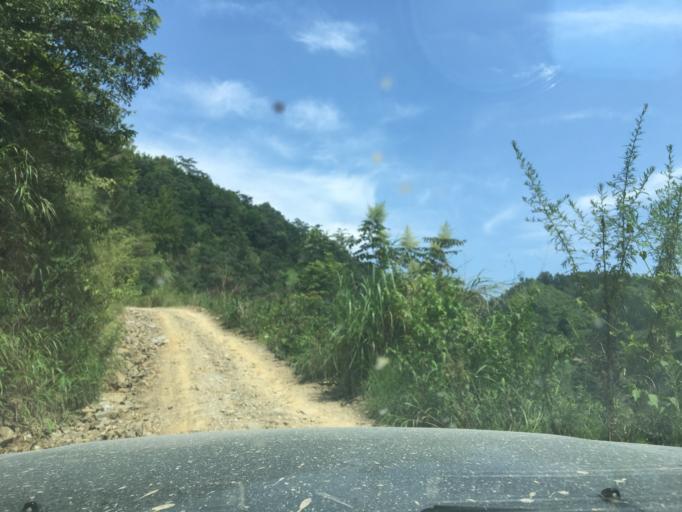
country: CN
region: Guangxi Zhuangzu Zizhiqu
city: Xinzhou
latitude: 25.0465
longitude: 105.8581
